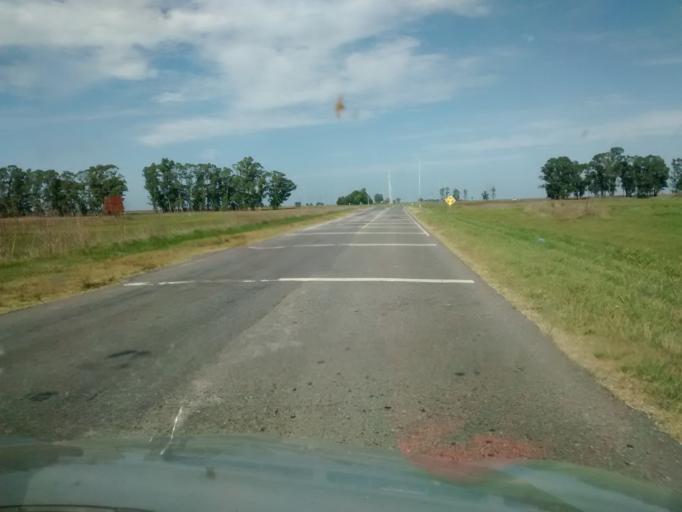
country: AR
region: Buenos Aires
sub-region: Partido de Ayacucho
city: Ayacucho
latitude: -37.2235
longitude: -58.4974
